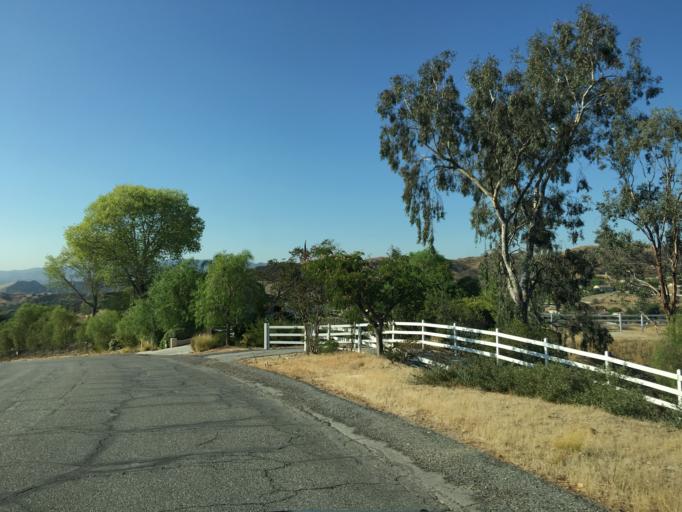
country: US
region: California
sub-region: Los Angeles County
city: Val Verde
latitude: 34.4695
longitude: -118.6658
